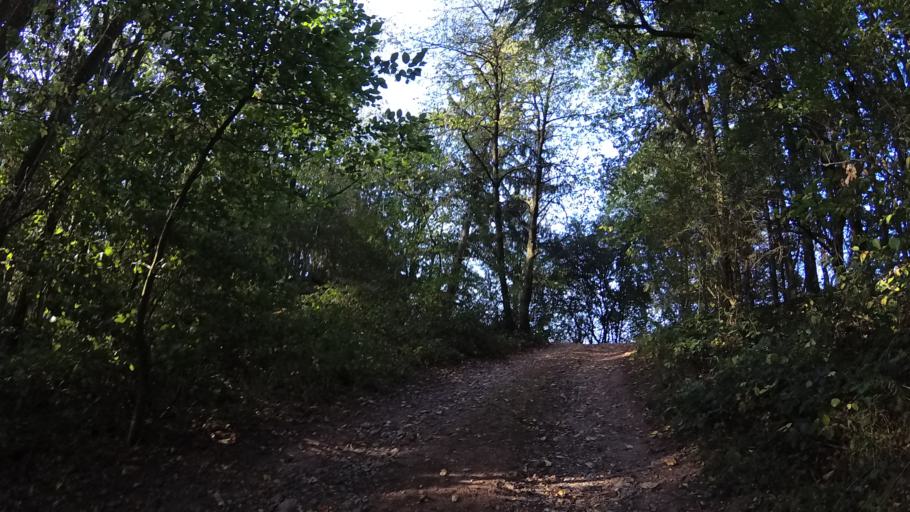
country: DE
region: Saarland
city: Ottweiler
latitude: 49.4189
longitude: 7.1762
